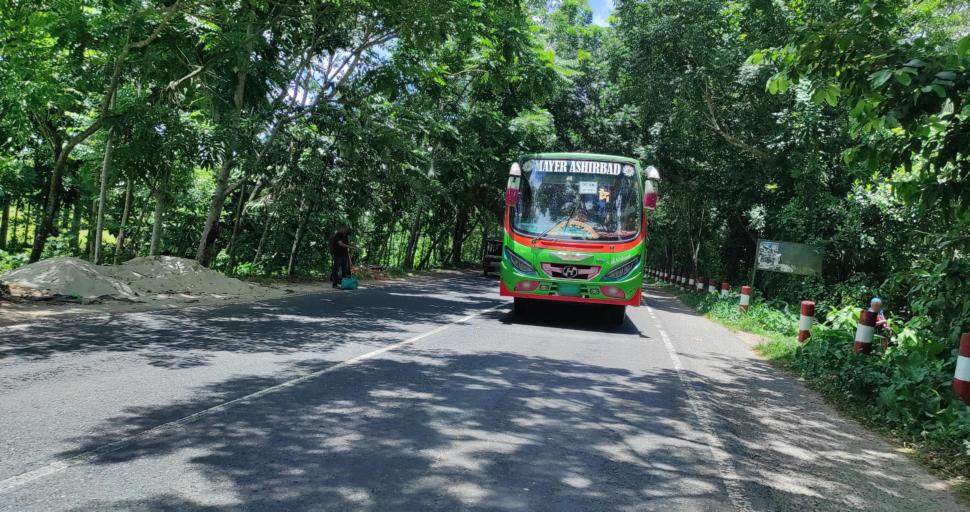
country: BD
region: Barisal
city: Gaurnadi
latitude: 22.8406
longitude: 90.2513
